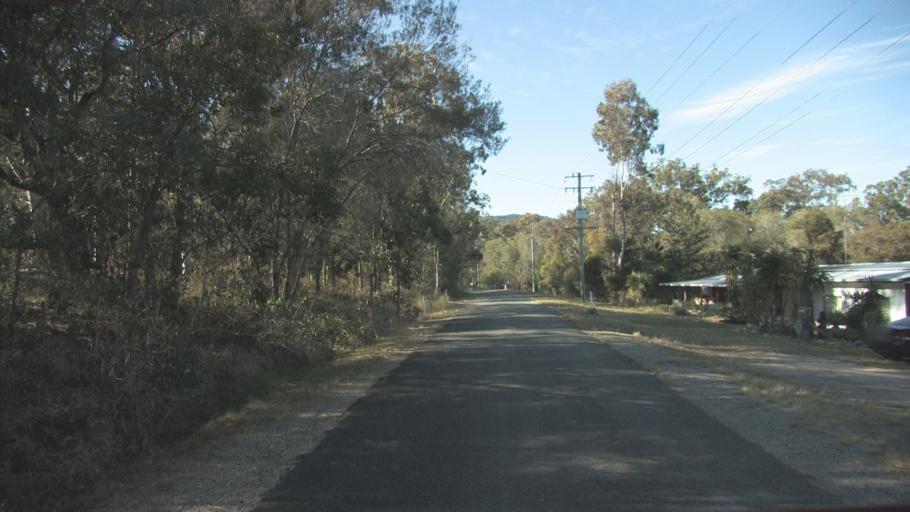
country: AU
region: Queensland
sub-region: Gold Coast
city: Ormeau Hills
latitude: -27.8199
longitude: 153.1749
